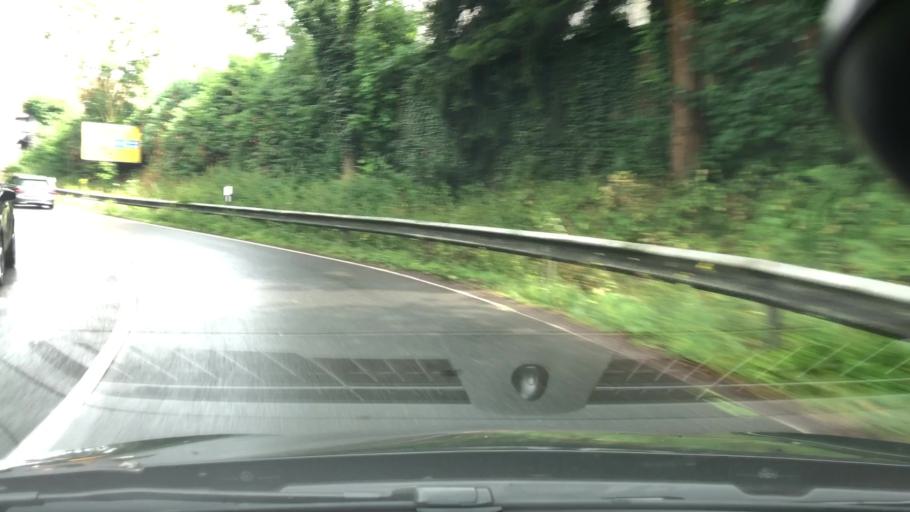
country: DE
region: North Rhine-Westphalia
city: Porta Westfalica
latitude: 52.2337
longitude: 8.9385
